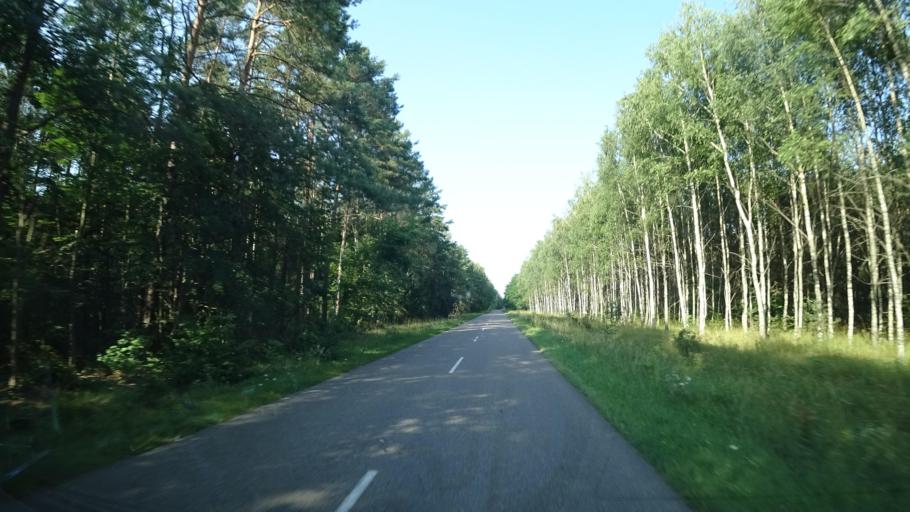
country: PL
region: Pomeranian Voivodeship
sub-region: Powiat czluchowski
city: Rzeczenica
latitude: 53.7708
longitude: 17.1491
